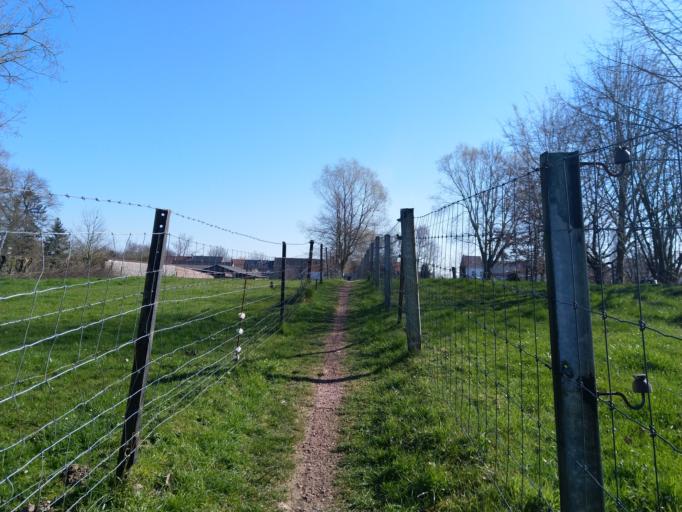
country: BE
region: Wallonia
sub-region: Province du Hainaut
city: Lens
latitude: 50.5517
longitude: 3.8990
